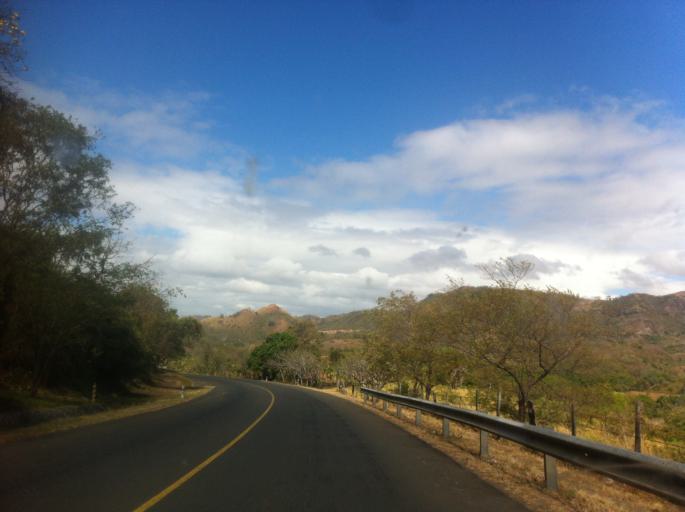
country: NI
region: Chontales
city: Acoyapa
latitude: 12.0080
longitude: -85.2280
